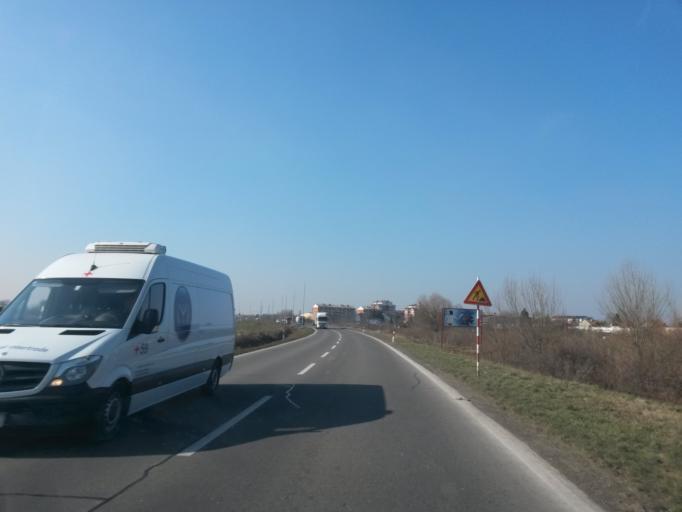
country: HR
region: Osjecko-Baranjska
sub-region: Grad Osijek
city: Osijek
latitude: 45.5407
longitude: 18.7199
